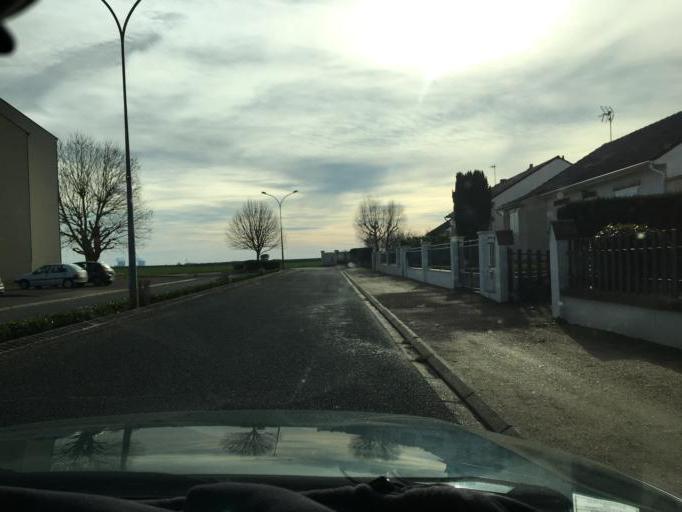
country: FR
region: Centre
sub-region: Departement du Loiret
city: Beaugency
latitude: 47.7809
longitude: 1.6160
